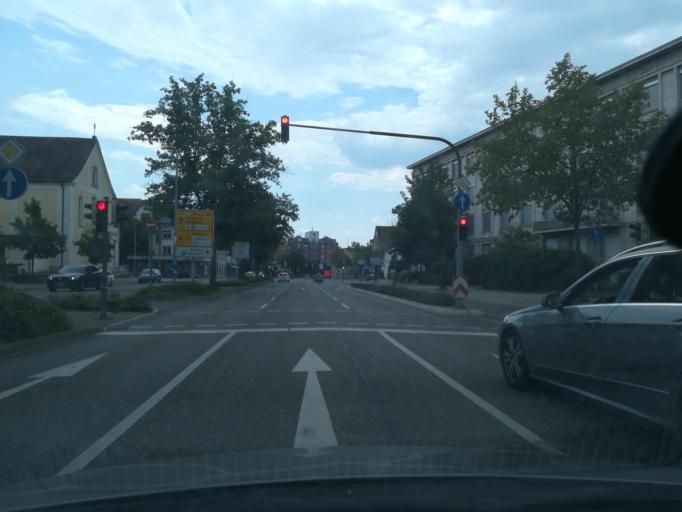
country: DE
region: Baden-Wuerttemberg
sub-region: Freiburg Region
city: Singen
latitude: 47.7619
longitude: 8.8344
